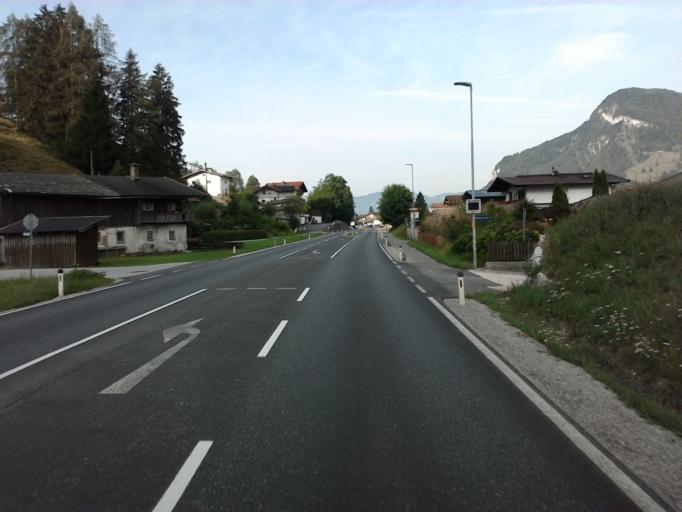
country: AT
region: Tyrol
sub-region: Politischer Bezirk Kitzbuhel
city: Kirchdorf in Tirol
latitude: 47.5554
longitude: 12.4567
